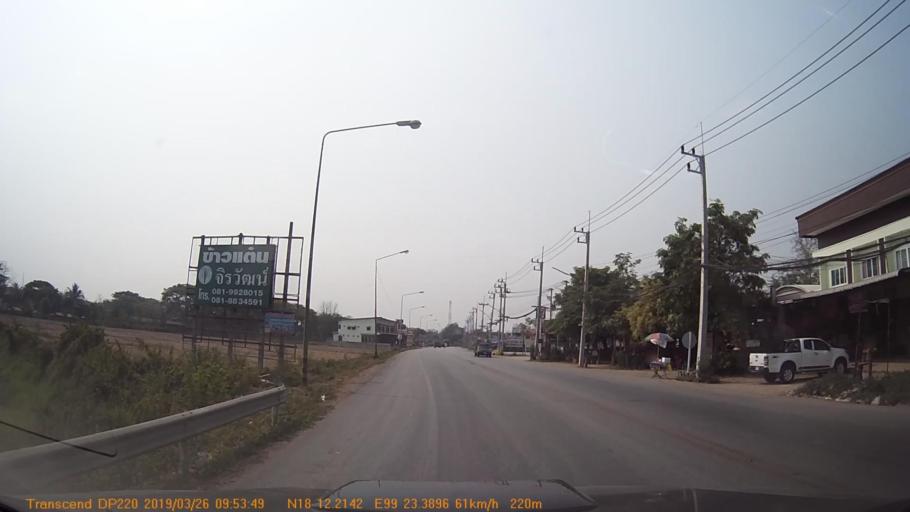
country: TH
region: Lampang
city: Ko Kha
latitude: 18.2034
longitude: 99.3898
